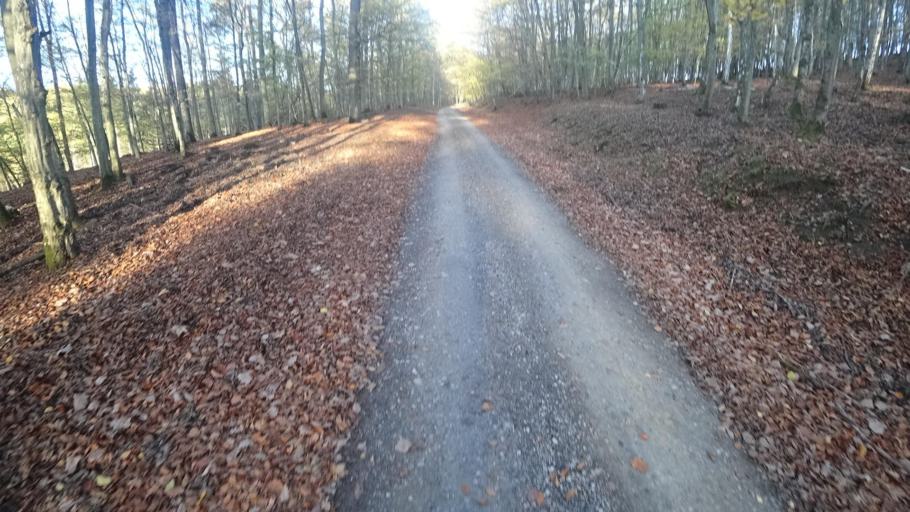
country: DE
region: Rheinland-Pfalz
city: Altenahr
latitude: 50.5374
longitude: 6.9770
